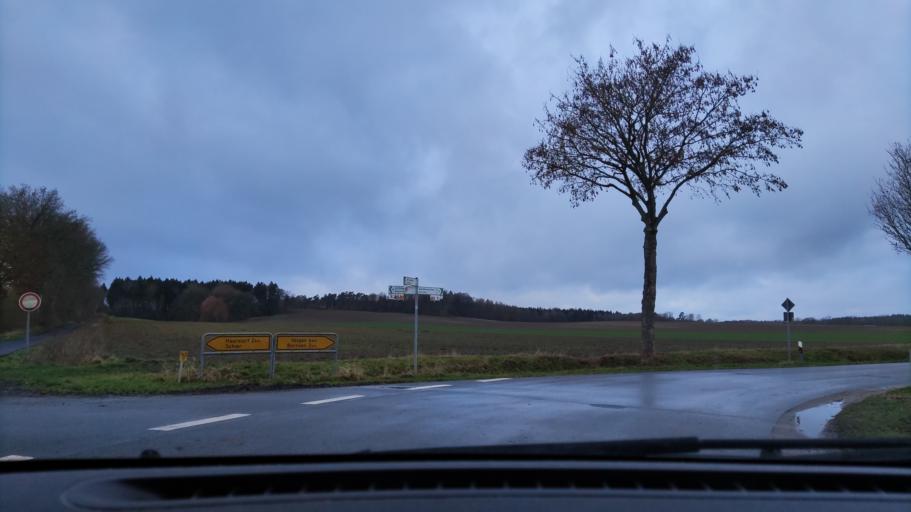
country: DE
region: Lower Saxony
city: Natendorf
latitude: 53.0846
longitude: 10.4448
